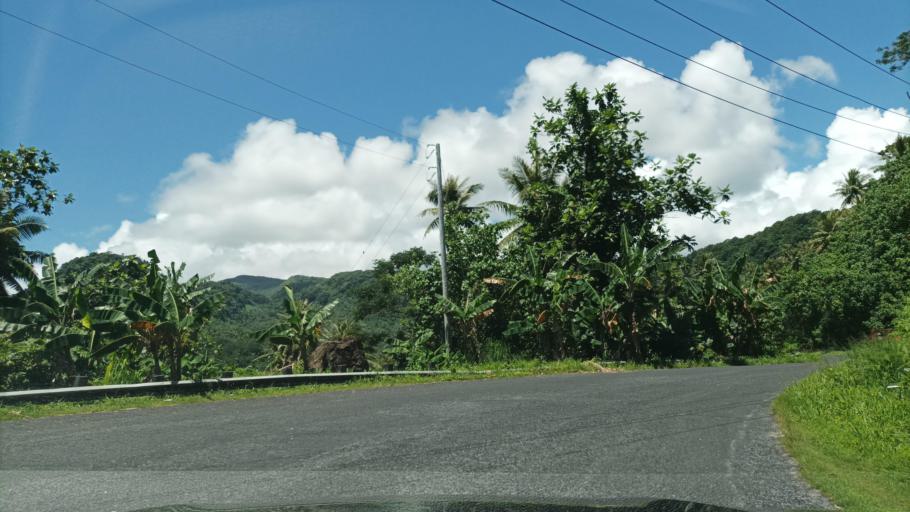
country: FM
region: Pohnpei
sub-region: Kolonia Municipality
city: Kolonia
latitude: 6.9680
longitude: 158.2619
